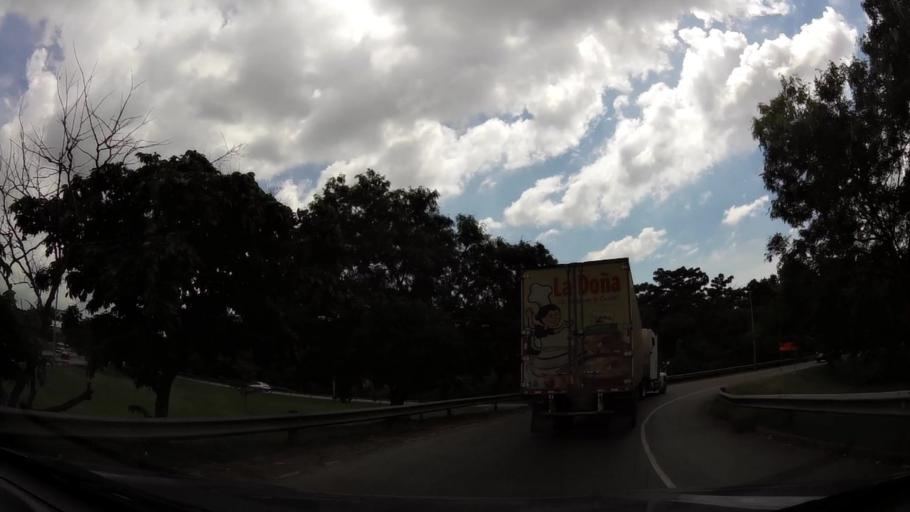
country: PA
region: Panama
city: Tocumen
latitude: 9.0694
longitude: -79.4030
